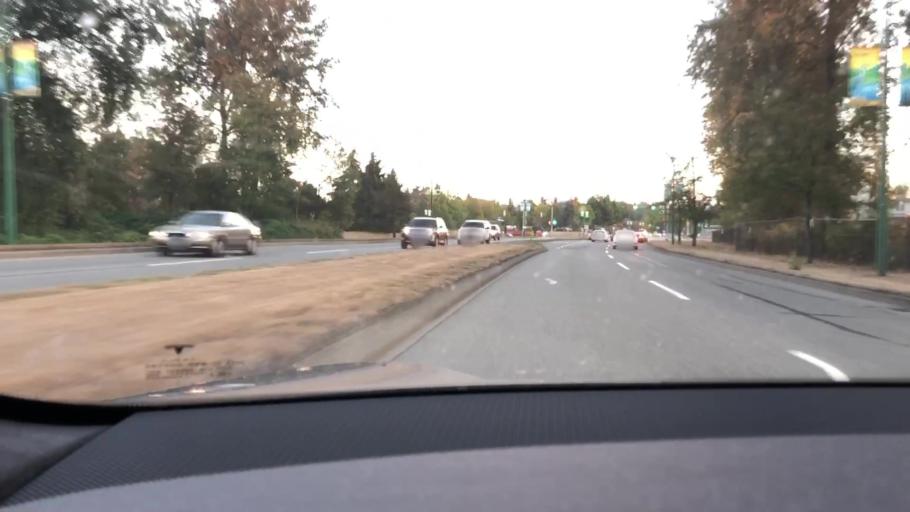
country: CA
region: British Columbia
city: Burnaby
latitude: 49.2592
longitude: -122.9623
